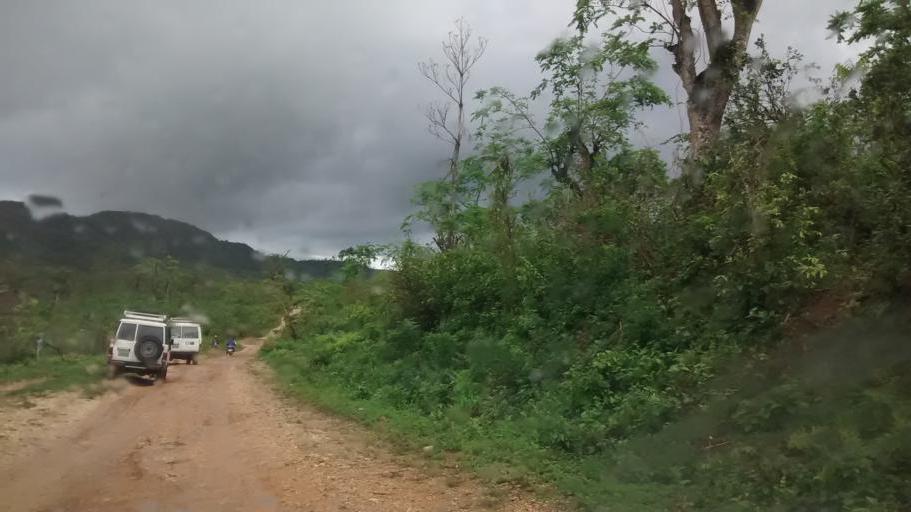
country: HT
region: Grandans
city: Corail
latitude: 18.5377
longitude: -73.9840
